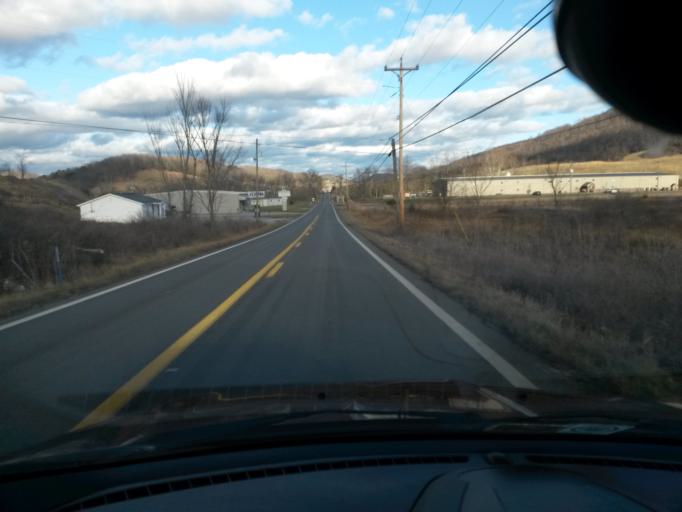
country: US
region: Virginia
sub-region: Giles County
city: Pearisburg
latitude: 37.4169
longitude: -80.7440
